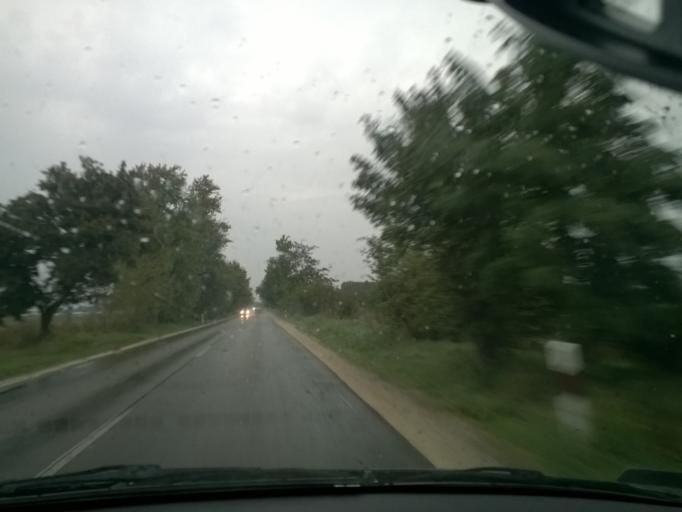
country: HU
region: Pest
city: Domsod
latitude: 47.0638
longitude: 19.0149
